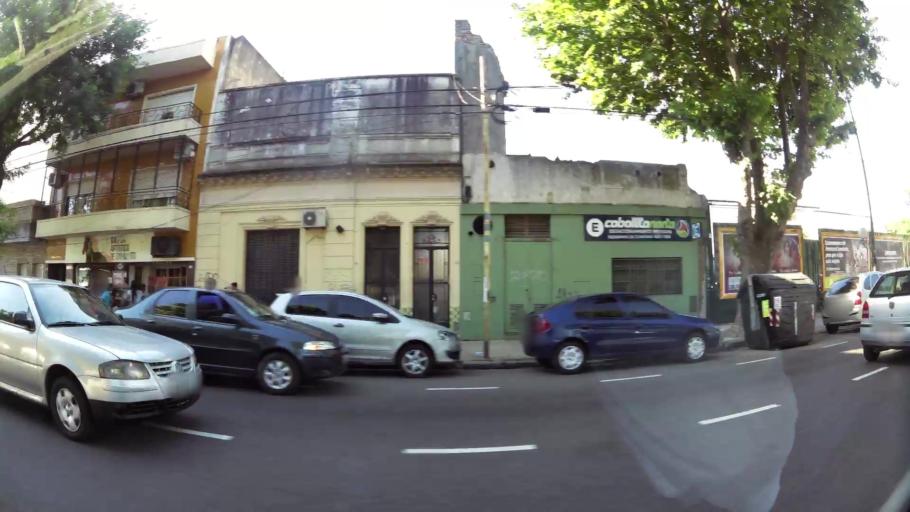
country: AR
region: Buenos Aires F.D.
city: Villa Santa Rita
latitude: -34.6192
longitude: -58.4509
